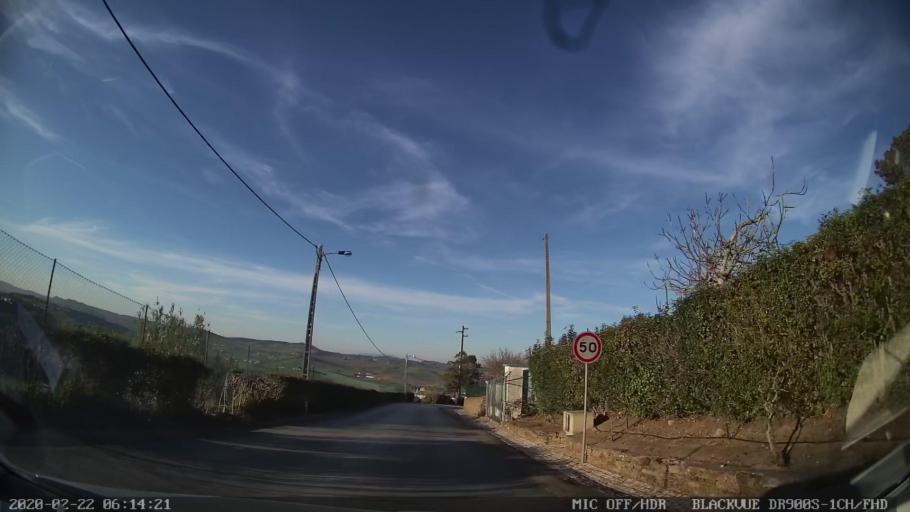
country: PT
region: Lisbon
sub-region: Vila Franca de Xira
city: Vila Franca de Xira
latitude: 38.9830
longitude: -9.0155
